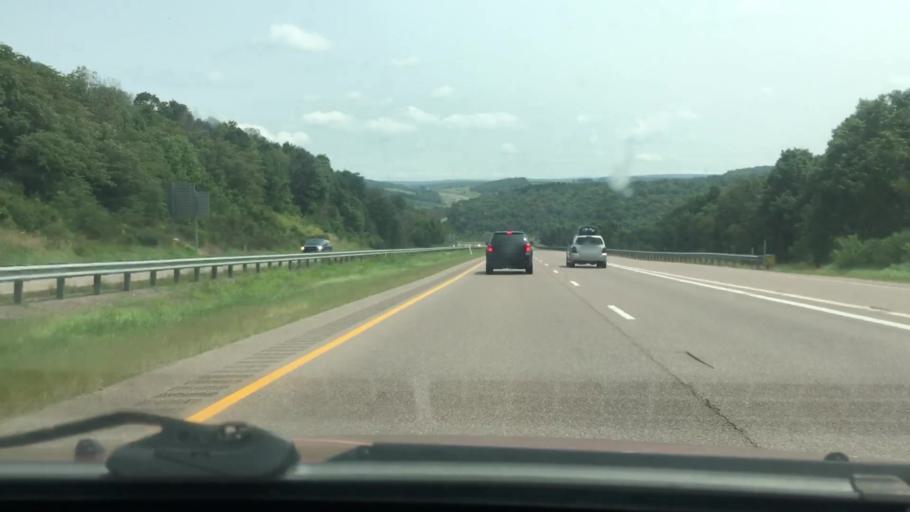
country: US
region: Pennsylvania
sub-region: Somerset County
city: Meyersdale
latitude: 39.6828
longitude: -79.0673
